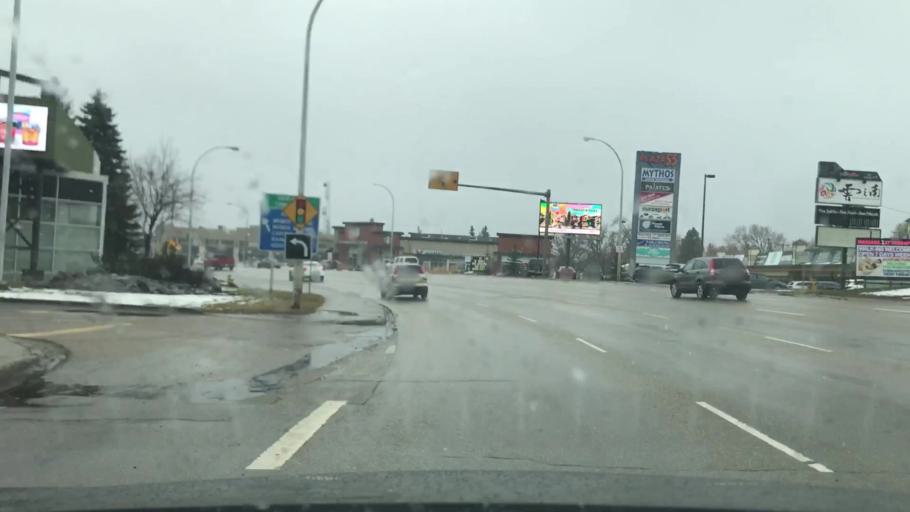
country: CA
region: Alberta
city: Edmonton
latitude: 53.4937
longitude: -113.4976
